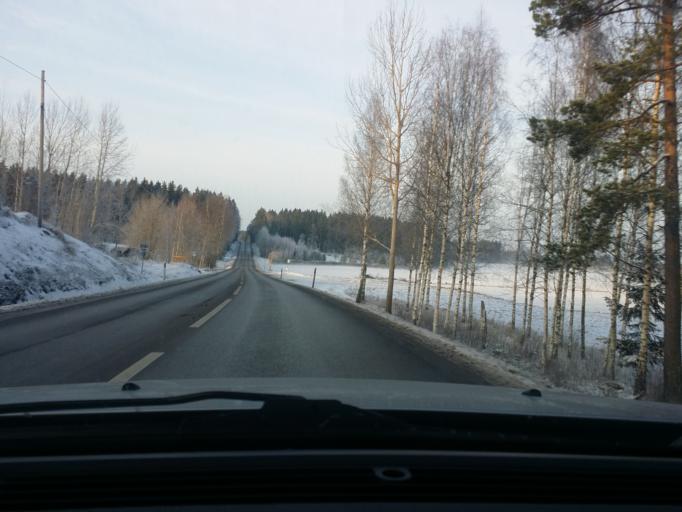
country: SE
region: OErebro
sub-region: Lindesbergs Kommun
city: Frovi
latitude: 59.5160
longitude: 15.3395
